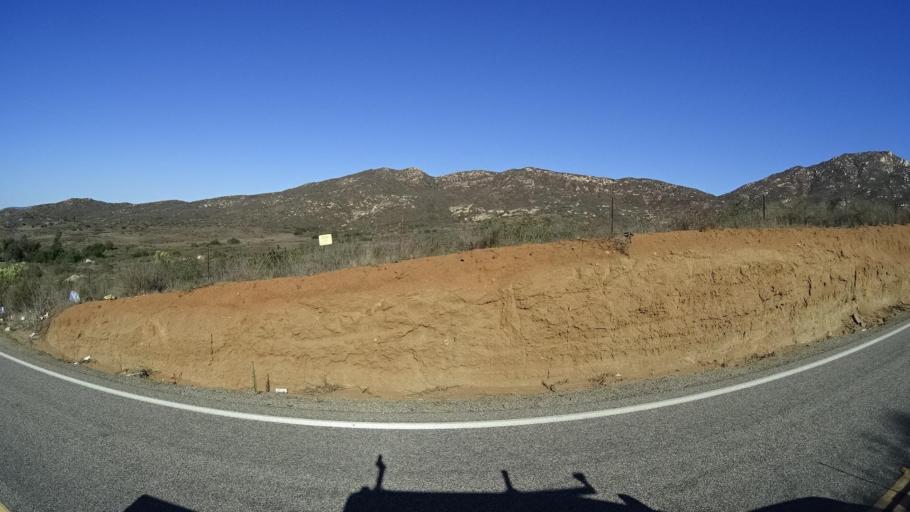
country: US
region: California
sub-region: San Diego County
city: Jamul
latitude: 32.6711
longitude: -116.7814
